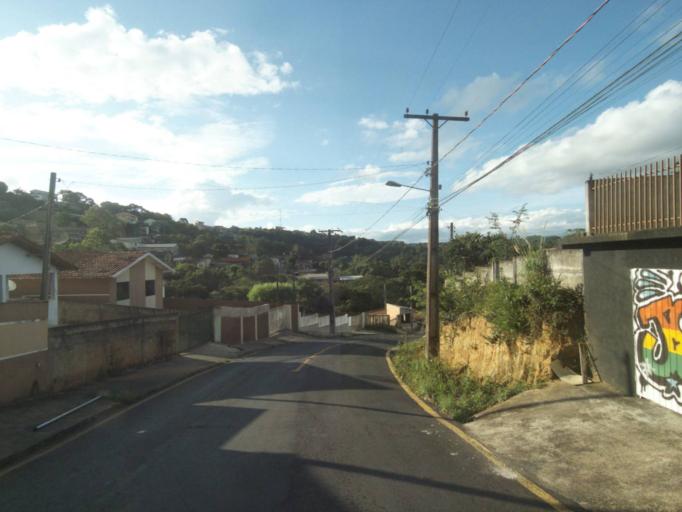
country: BR
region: Parana
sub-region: Telemaco Borba
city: Telemaco Borba
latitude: -24.3236
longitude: -50.6132
